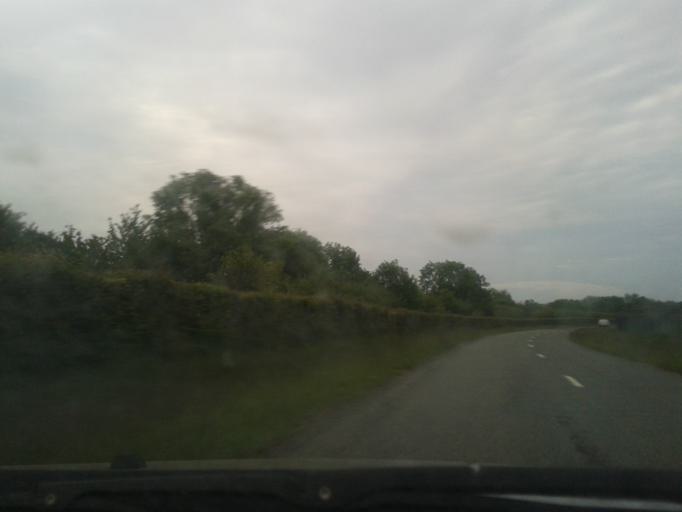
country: IE
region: Leinster
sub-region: Dublin City
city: Finglas
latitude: 53.4249
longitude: -6.3036
